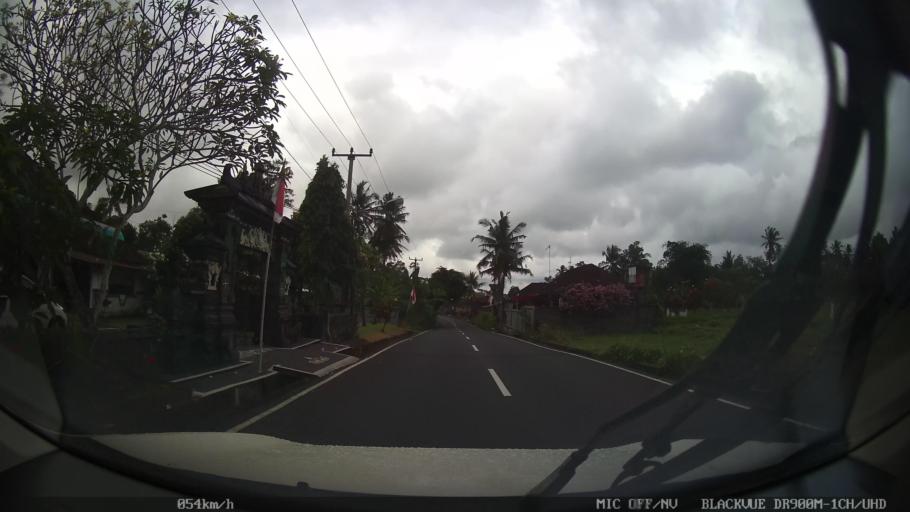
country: ID
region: Bali
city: Banjar Sayanbaleran
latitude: -8.5123
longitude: 115.1878
